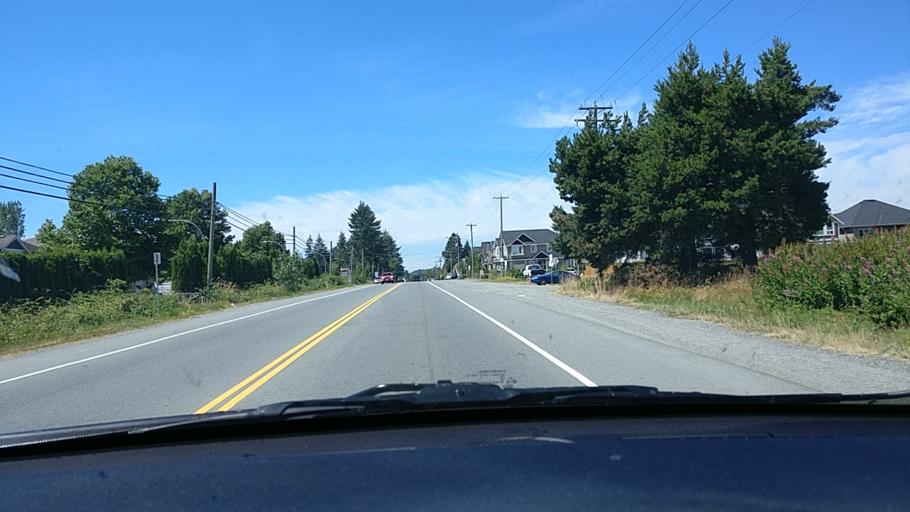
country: CA
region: British Columbia
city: Aldergrove
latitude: 49.0575
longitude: -122.4528
